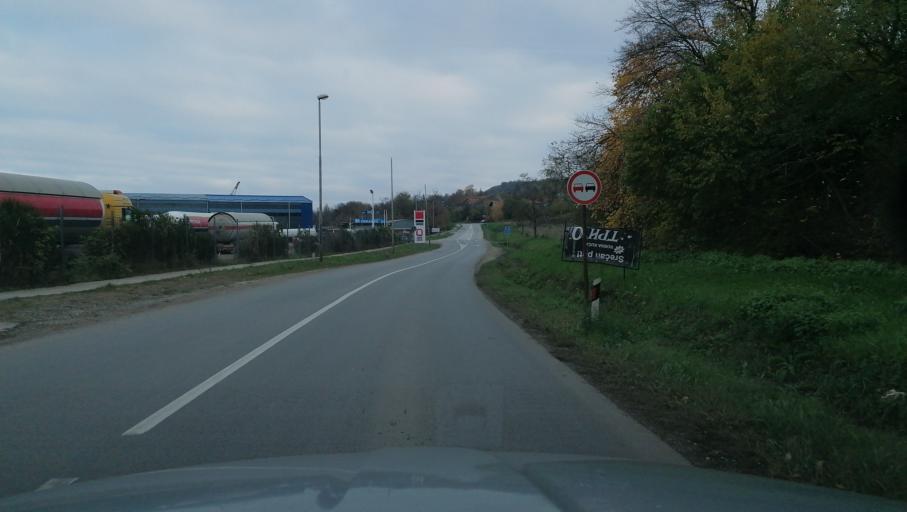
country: RS
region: Central Serbia
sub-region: Podunavski Okrug
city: Smederevo
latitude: 44.6603
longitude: 20.8915
